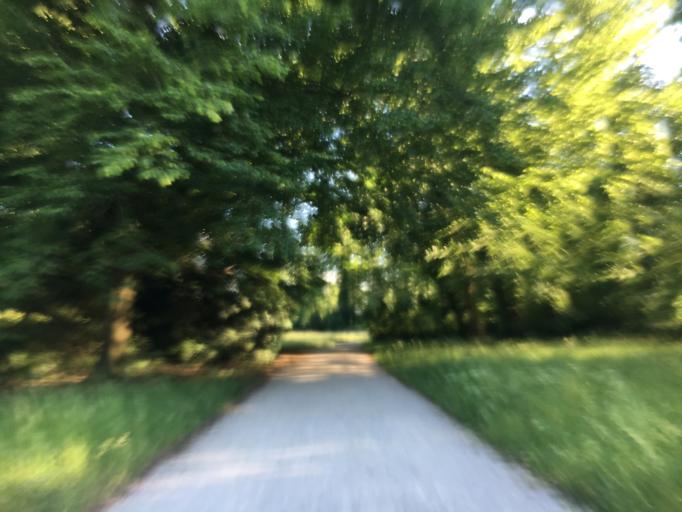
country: DE
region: Brandenburg
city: Potsdam
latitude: 52.4173
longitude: 13.0713
